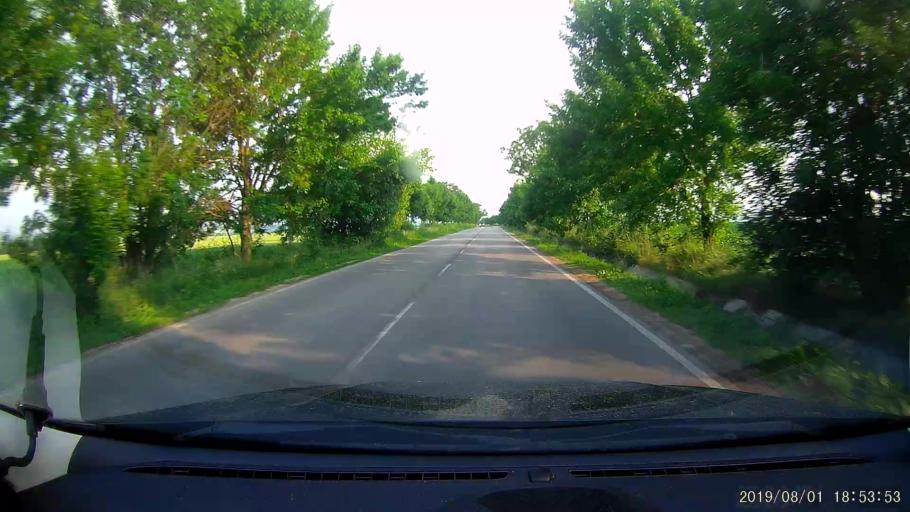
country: BG
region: Shumen
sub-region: Obshtina Shumen
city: Shumen
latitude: 43.2123
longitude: 26.9982
